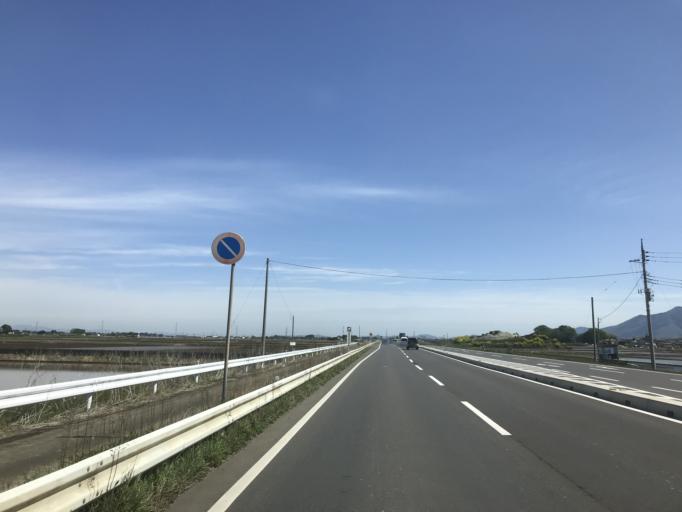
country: JP
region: Ibaraki
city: Ishige
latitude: 36.1412
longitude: 139.9877
